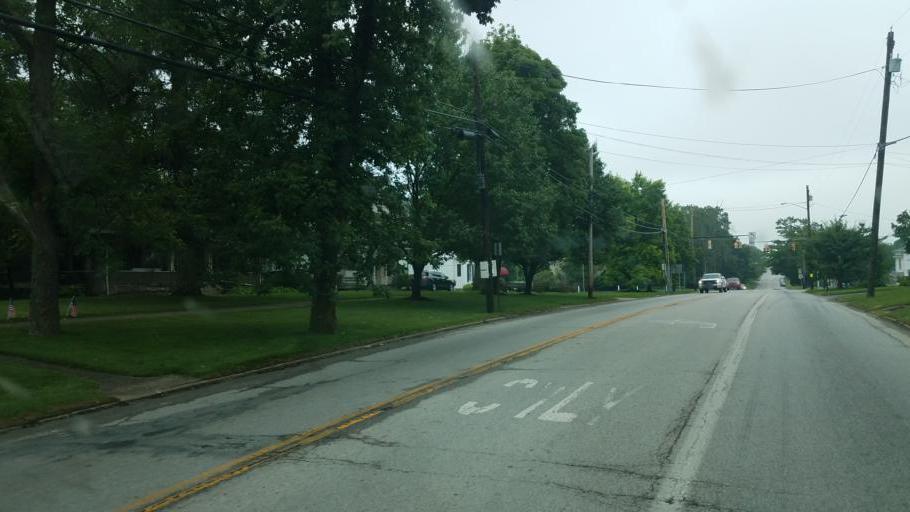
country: US
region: Ohio
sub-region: Highland County
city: Hillsboro
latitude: 39.2095
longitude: -83.6098
